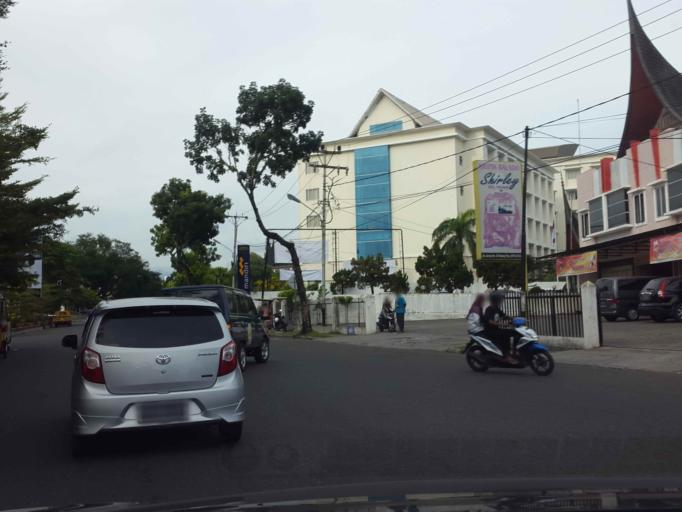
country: ID
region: West Sumatra
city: Padang
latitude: -0.9572
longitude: 100.3557
